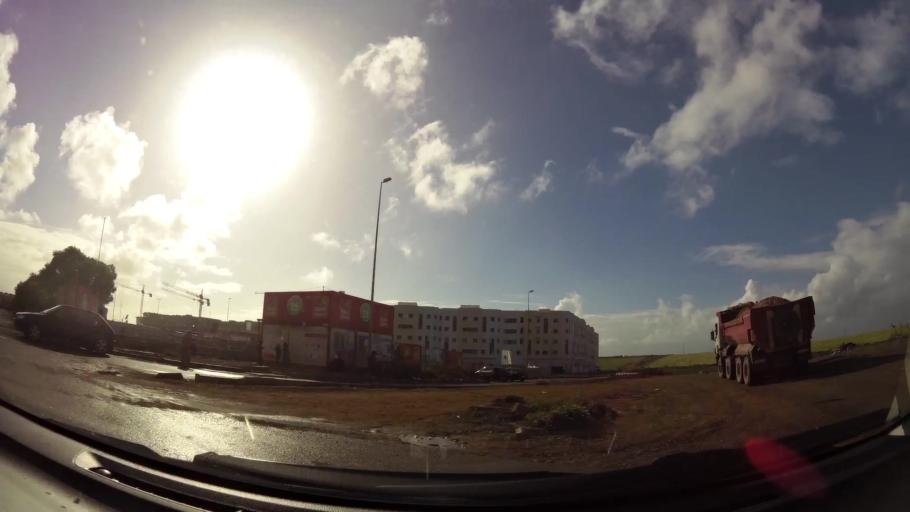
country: MA
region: Grand Casablanca
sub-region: Casablanca
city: Casablanca
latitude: 33.5578
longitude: -7.7040
